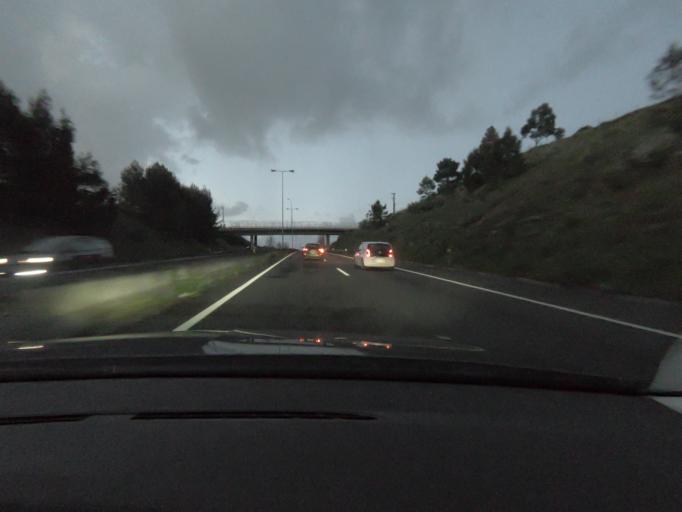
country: PT
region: Lisbon
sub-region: Oeiras
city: Porto Salvo
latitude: 38.7187
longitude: -9.2962
